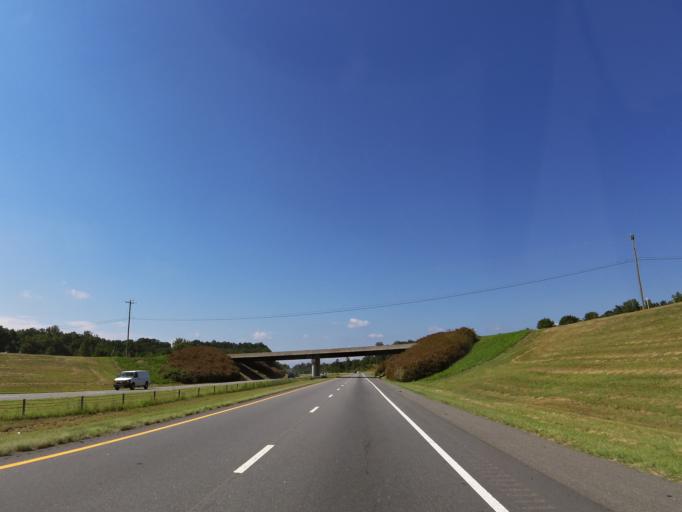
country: US
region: North Carolina
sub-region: Catawba County
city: Mountain View
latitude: 35.6785
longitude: -81.3396
